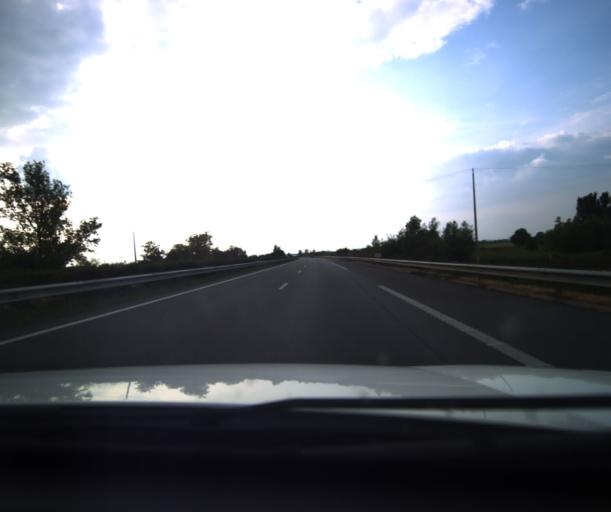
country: FR
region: Midi-Pyrenees
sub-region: Departement du Tarn-et-Garonne
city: Castelsarrasin
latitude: 44.0464
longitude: 1.1437
